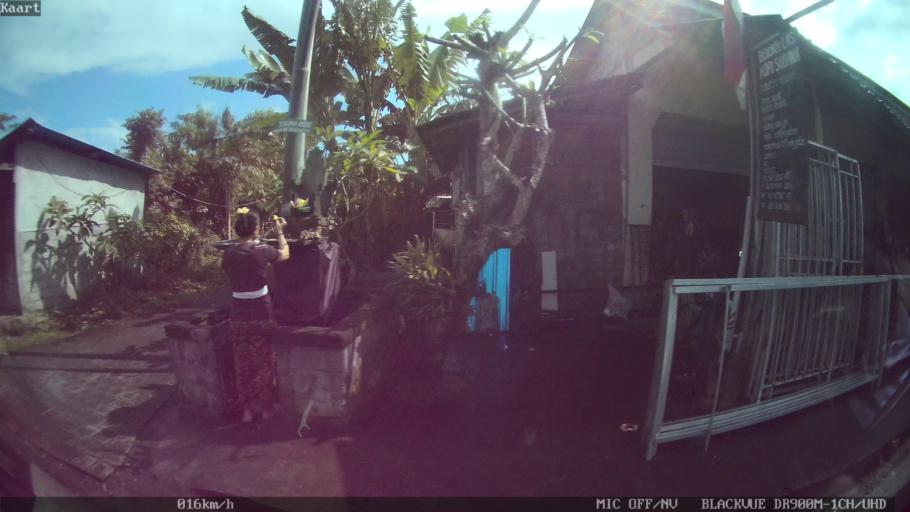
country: ID
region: Bali
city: Banjar Tebongkang
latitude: -8.5455
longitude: 115.2581
